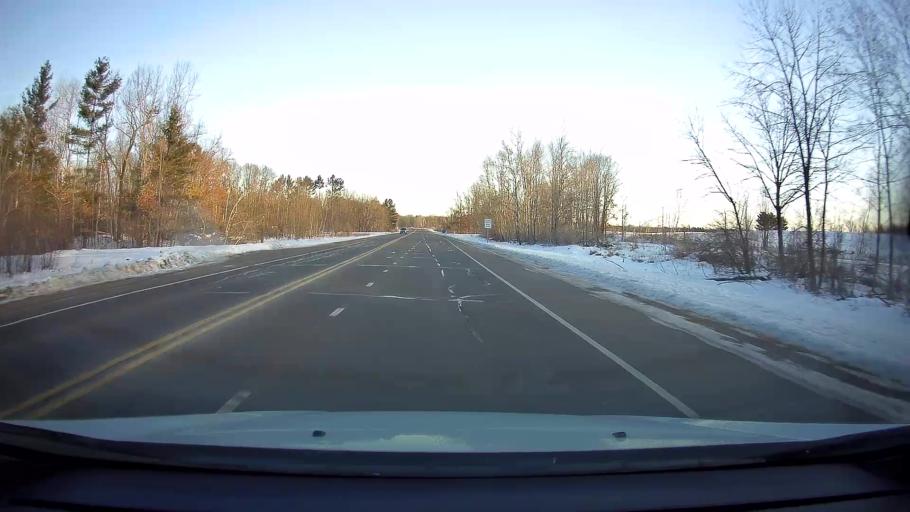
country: US
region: Wisconsin
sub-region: Barron County
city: Turtle Lake
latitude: 45.4251
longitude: -92.1298
